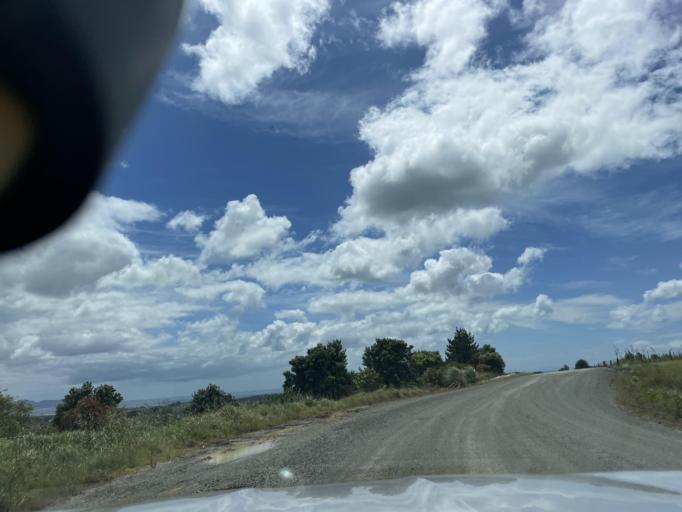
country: NZ
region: Auckland
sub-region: Auckland
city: Wellsford
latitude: -36.1711
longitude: 174.5596
